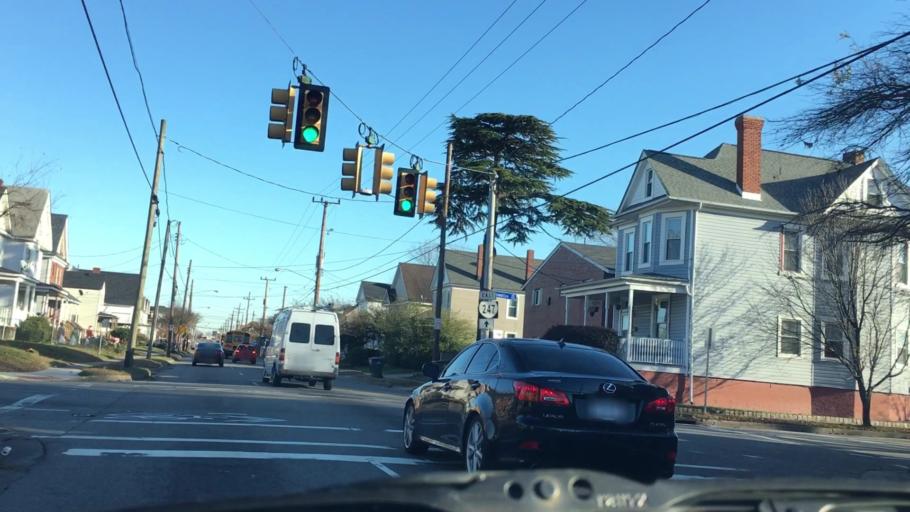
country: US
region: Virginia
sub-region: City of Norfolk
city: Norfolk
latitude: 36.8721
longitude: -76.2871
